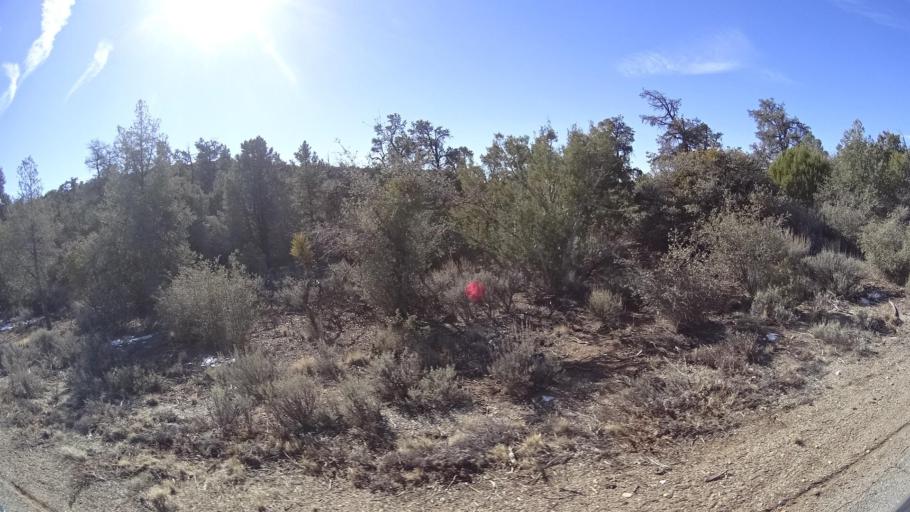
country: US
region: California
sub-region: Kern County
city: Pine Mountain Club
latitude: 34.8689
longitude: -119.2626
